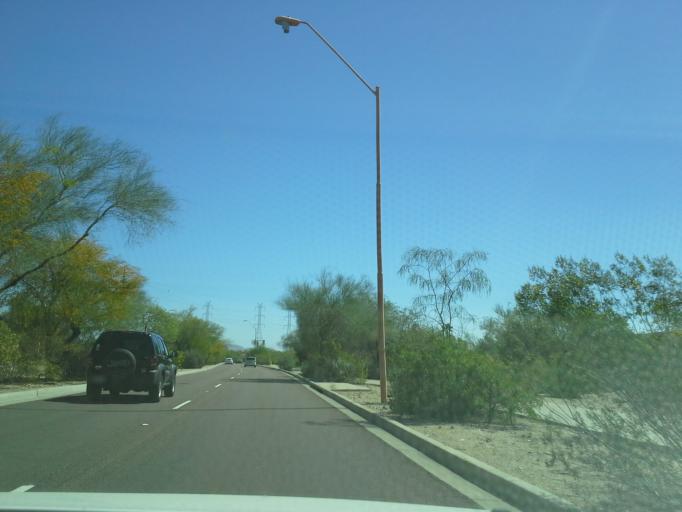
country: US
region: Arizona
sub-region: Maricopa County
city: Scottsdale
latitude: 33.6005
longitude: -111.8484
